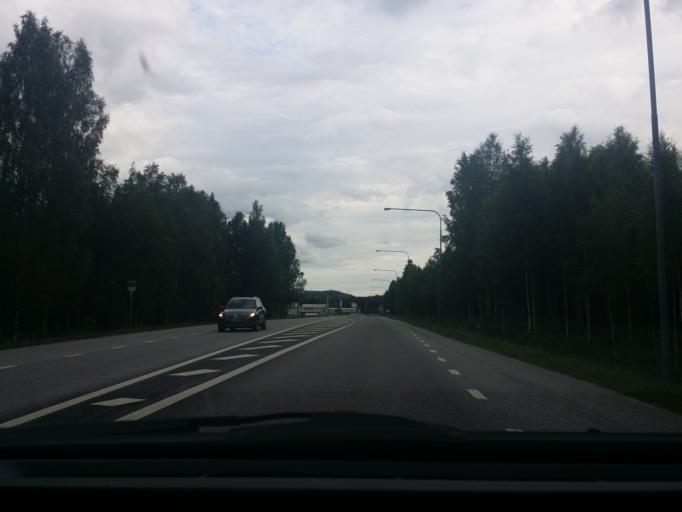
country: SE
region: OErebro
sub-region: Nora Kommun
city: Nora
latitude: 59.5148
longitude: 15.0224
